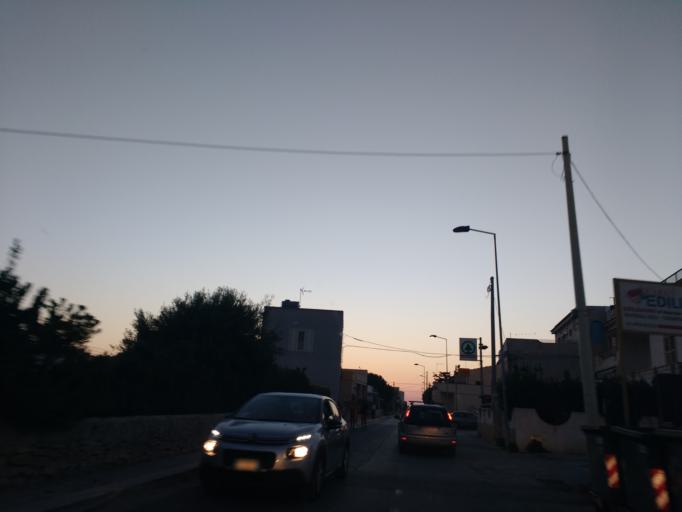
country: IT
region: Sicily
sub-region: Ragusa
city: Cava d'Aliga
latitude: 36.7252
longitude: 14.6911
